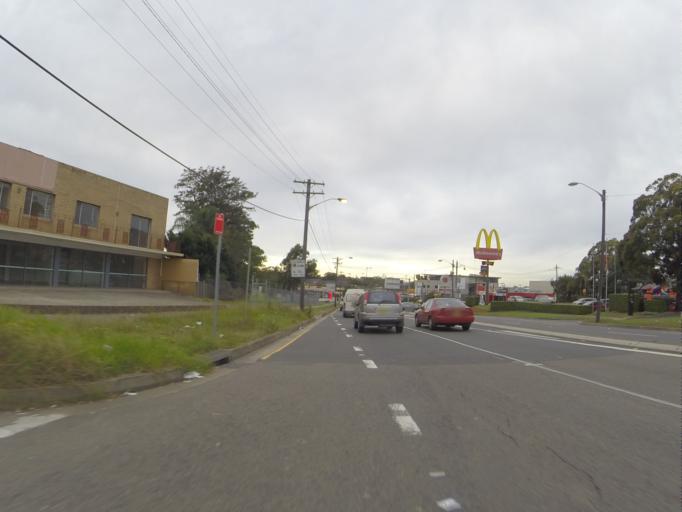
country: AU
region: New South Wales
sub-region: Strathfield
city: Strathfield South
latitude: -33.8867
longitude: 151.0719
